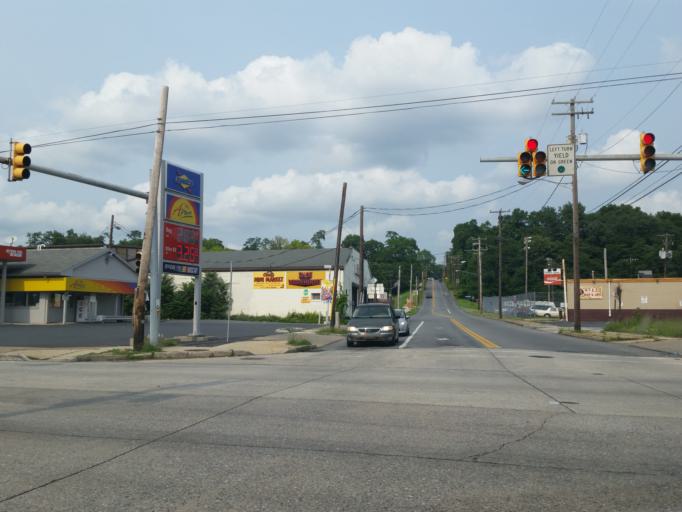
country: US
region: Pennsylvania
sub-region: Dauphin County
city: Harrisburg
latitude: 40.2724
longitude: -76.8774
